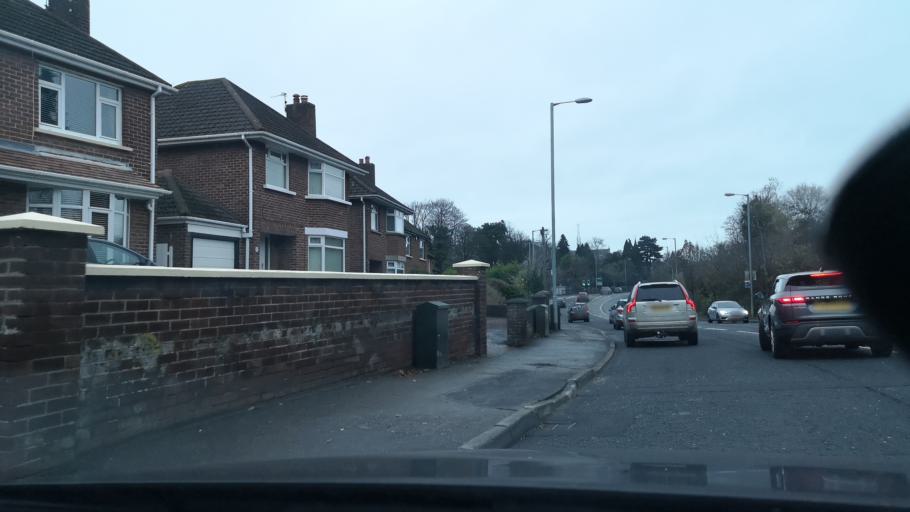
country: GB
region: Northern Ireland
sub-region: Castlereagh District
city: Castlereagh
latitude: 54.5890
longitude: -5.8560
